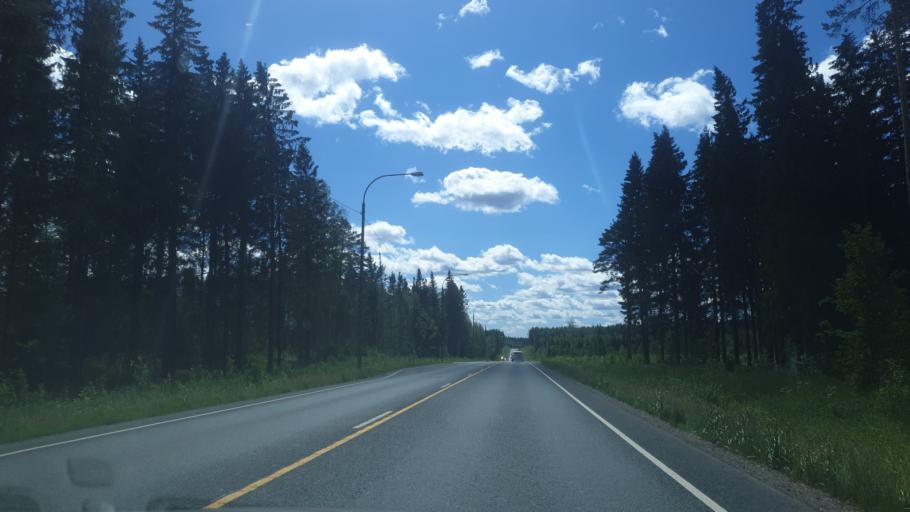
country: FI
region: Northern Savo
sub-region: Varkaus
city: Leppaevirta
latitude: 62.6204
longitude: 27.6223
